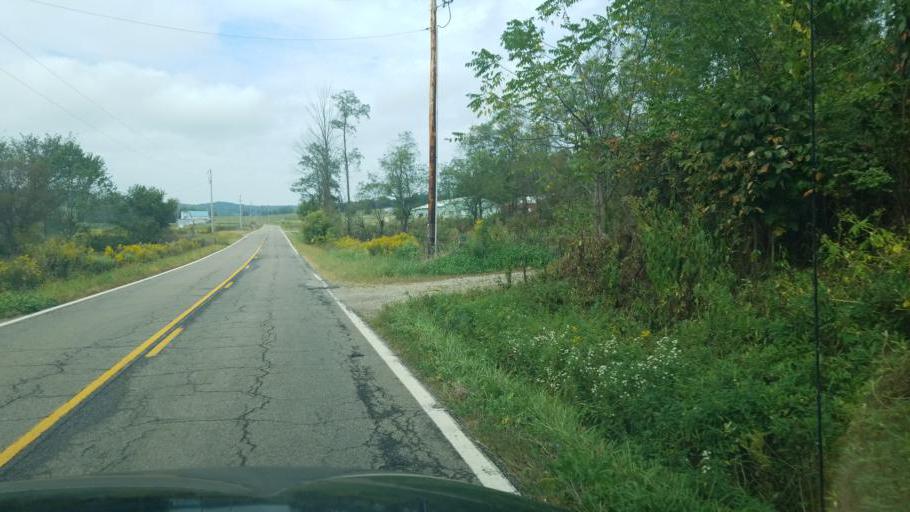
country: US
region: Ohio
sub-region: Perry County
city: Somerset
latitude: 39.9520
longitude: -82.2584
